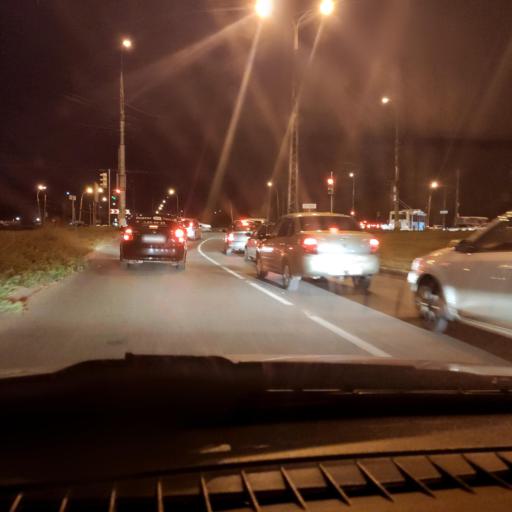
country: RU
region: Samara
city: Tol'yatti
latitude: 53.5529
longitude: 49.3032
